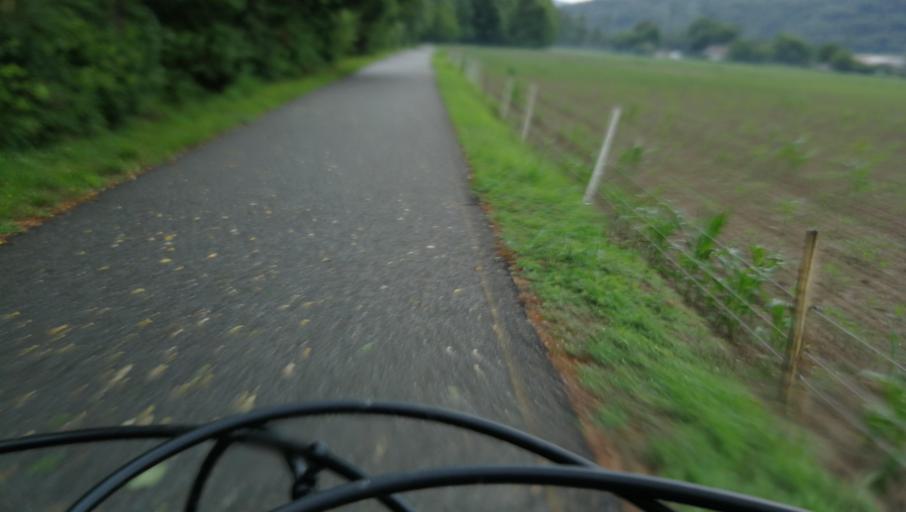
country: IT
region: Lombardy
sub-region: Provincia di Varese
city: Laveno
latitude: 45.9008
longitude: 8.6395
